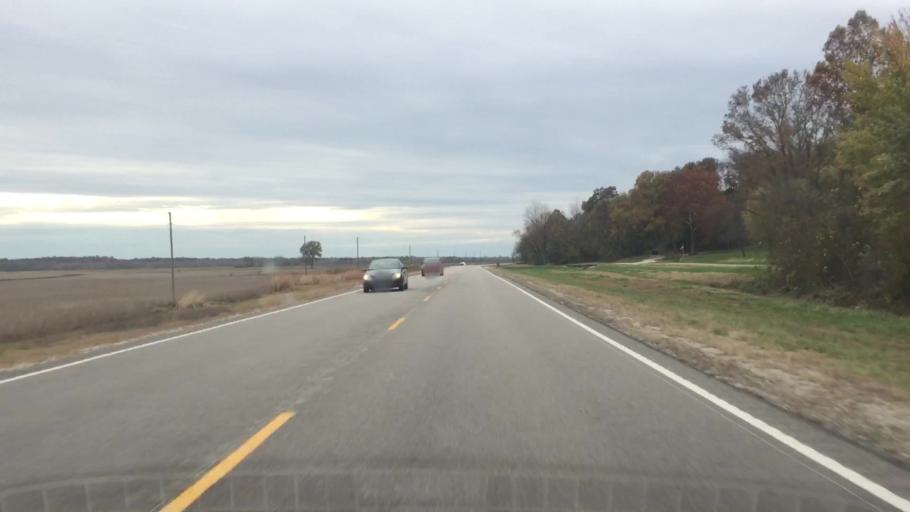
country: US
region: Missouri
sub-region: Callaway County
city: Holts Summit
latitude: 38.5812
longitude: -92.0770
